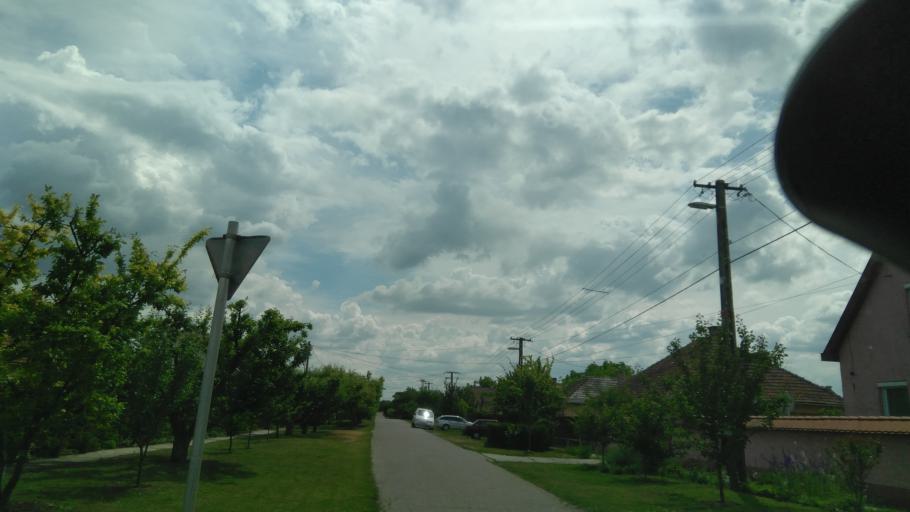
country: HU
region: Bekes
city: Mezohegyes
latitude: 46.3252
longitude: 20.8132
